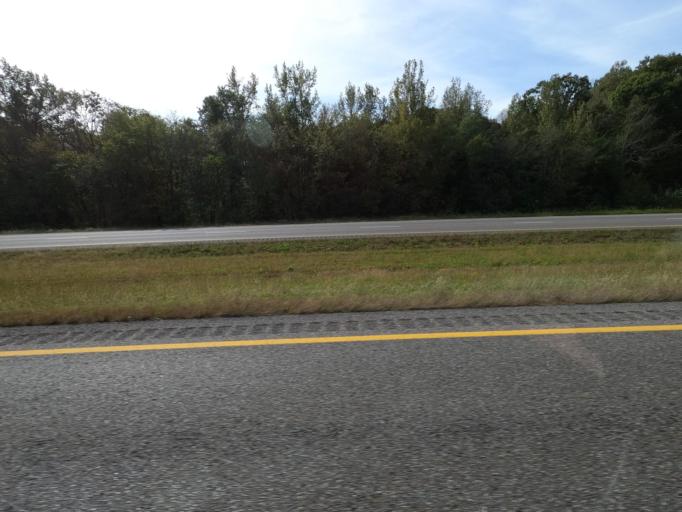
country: US
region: Tennessee
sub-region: Humphreys County
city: New Johnsonville
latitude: 35.8641
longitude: -87.9112
